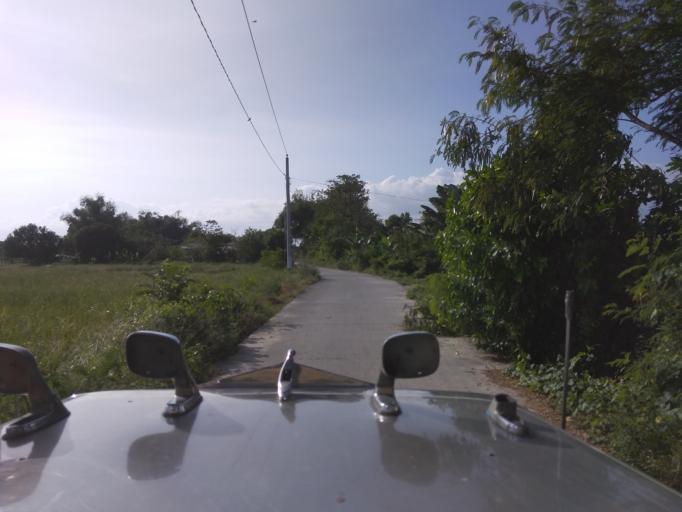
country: PH
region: Central Luzon
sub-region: Province of Pampanga
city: Malino
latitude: 15.1003
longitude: 120.6943
